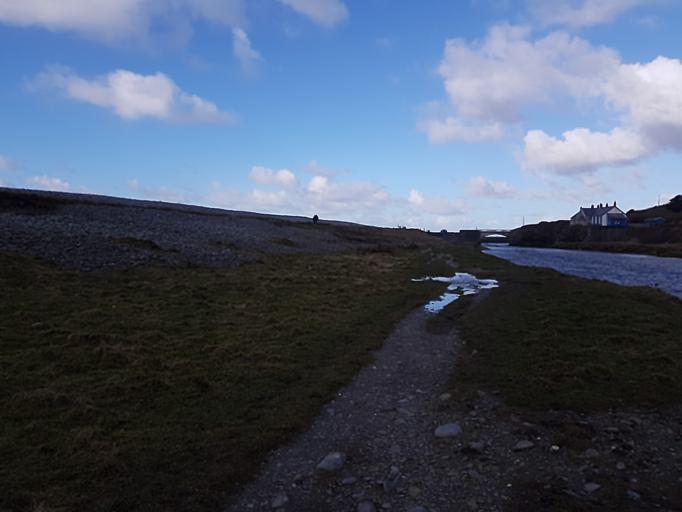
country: GB
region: Wales
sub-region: County of Ceredigion
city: Aberystwyth
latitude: 52.4034
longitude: -4.0884
